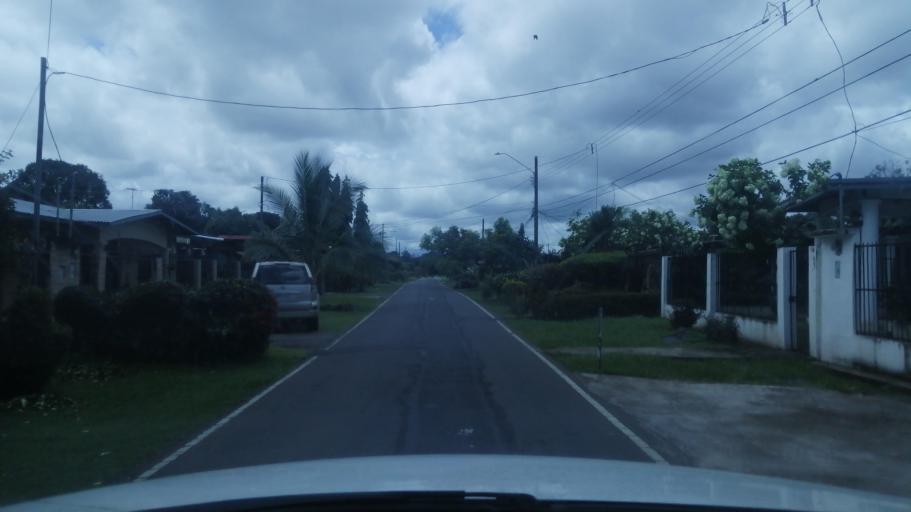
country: PA
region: Chiriqui
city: David
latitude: 8.4152
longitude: -82.4282
